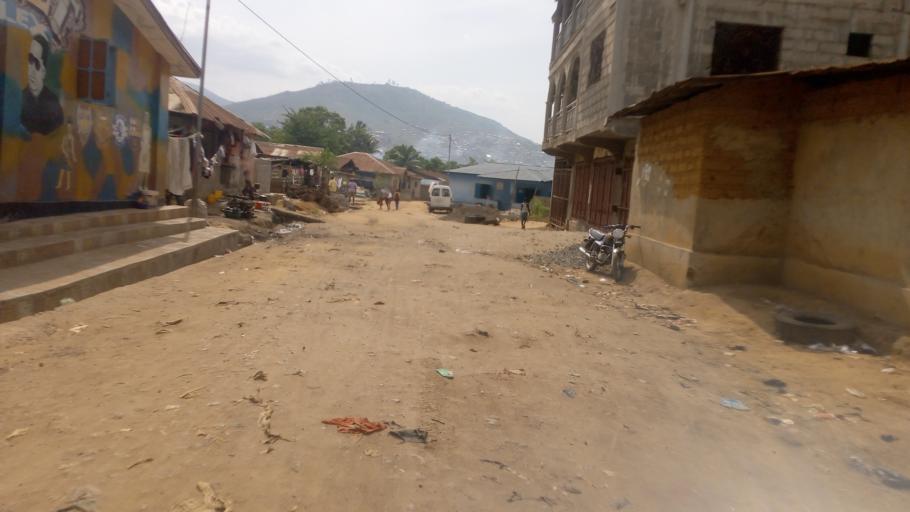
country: SL
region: Western Area
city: Waterloo
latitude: 8.3269
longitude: -13.0645
